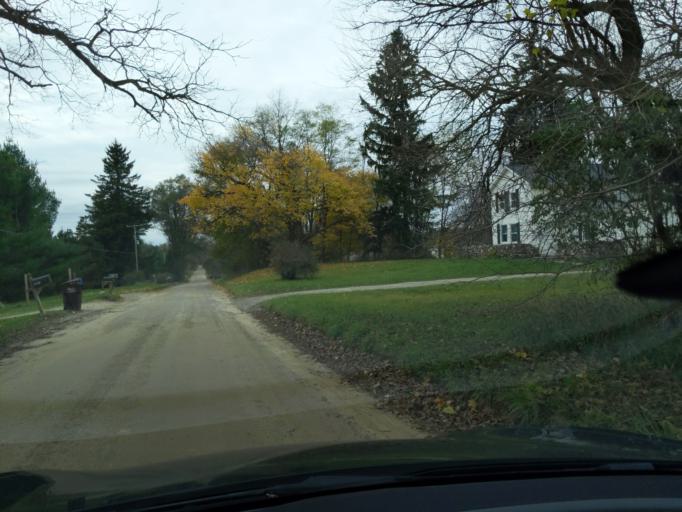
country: US
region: Michigan
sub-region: Eaton County
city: Eaton Rapids
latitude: 42.5532
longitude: -84.6066
